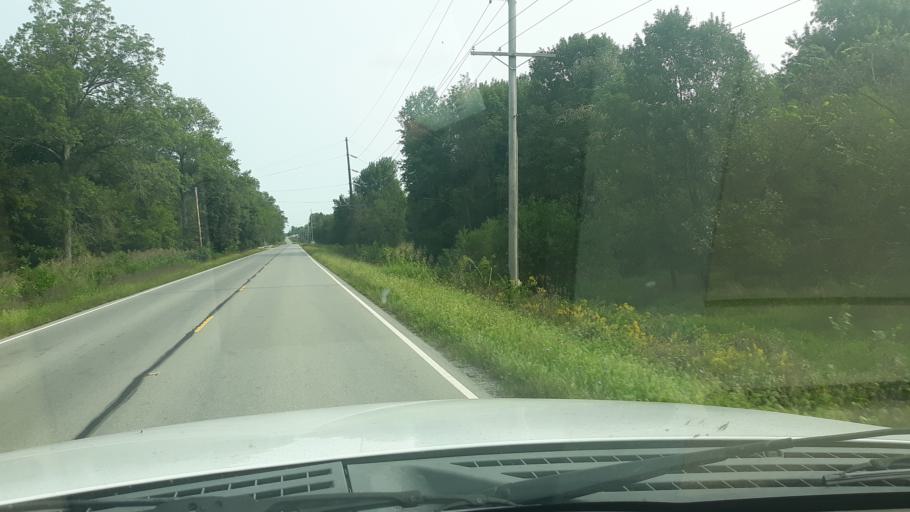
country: US
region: Illinois
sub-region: White County
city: Norris City
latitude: 37.9402
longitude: -88.3433
